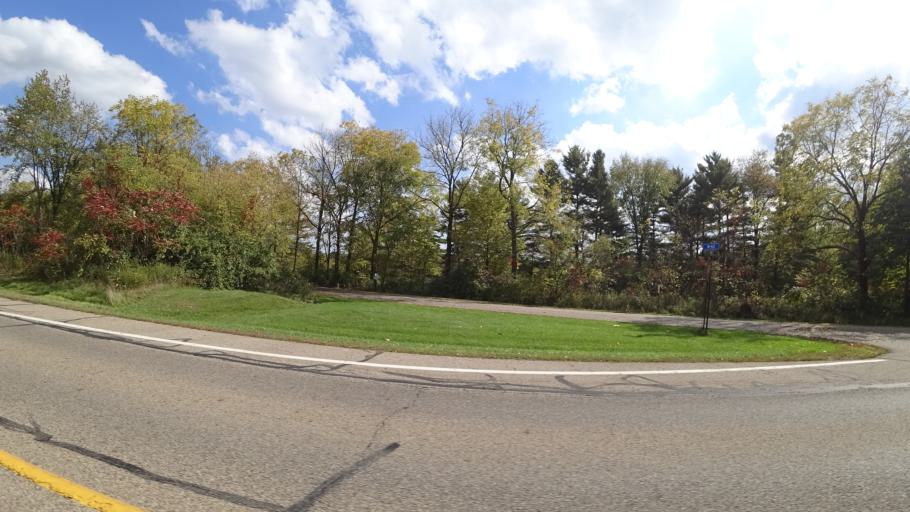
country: US
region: Michigan
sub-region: Branch County
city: Union City
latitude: 42.1038
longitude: -85.0894
